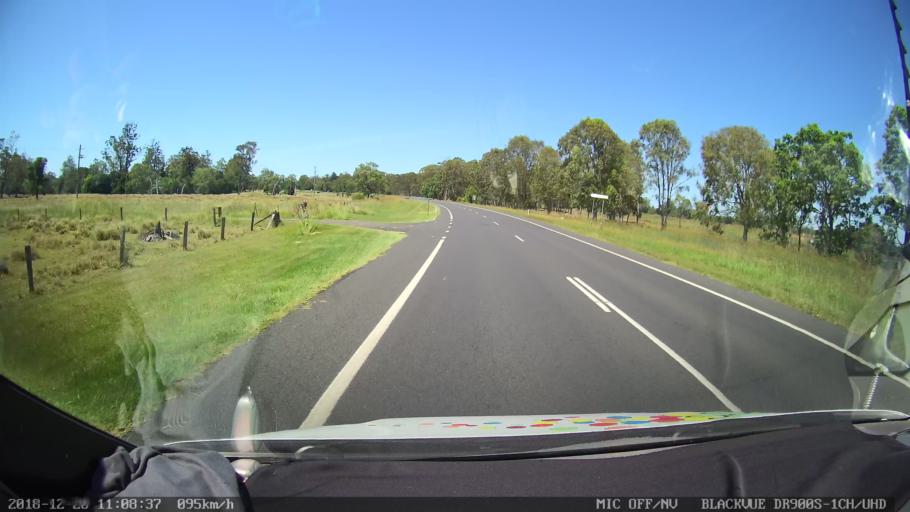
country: AU
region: New South Wales
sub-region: Richmond Valley
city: Casino
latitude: -28.9246
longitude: 153.0052
